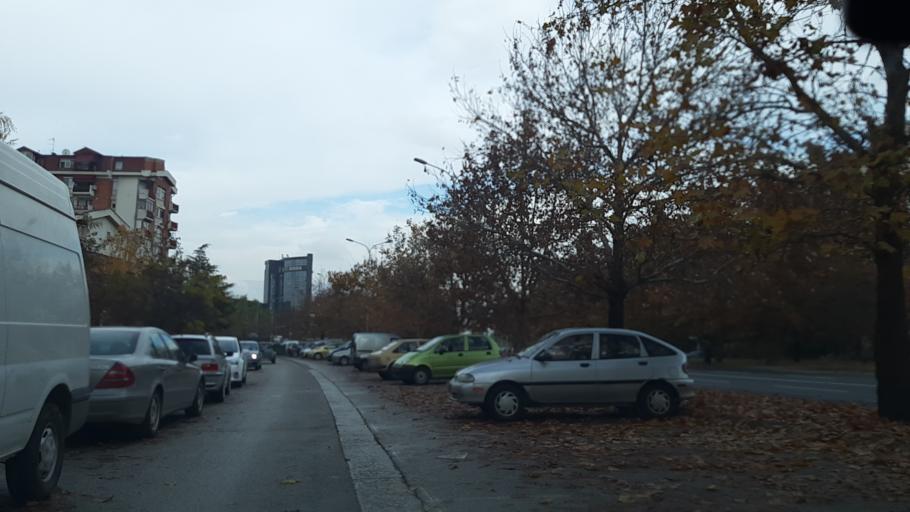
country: MK
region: Kisela Voda
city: Usje
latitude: 41.9902
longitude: 21.4638
